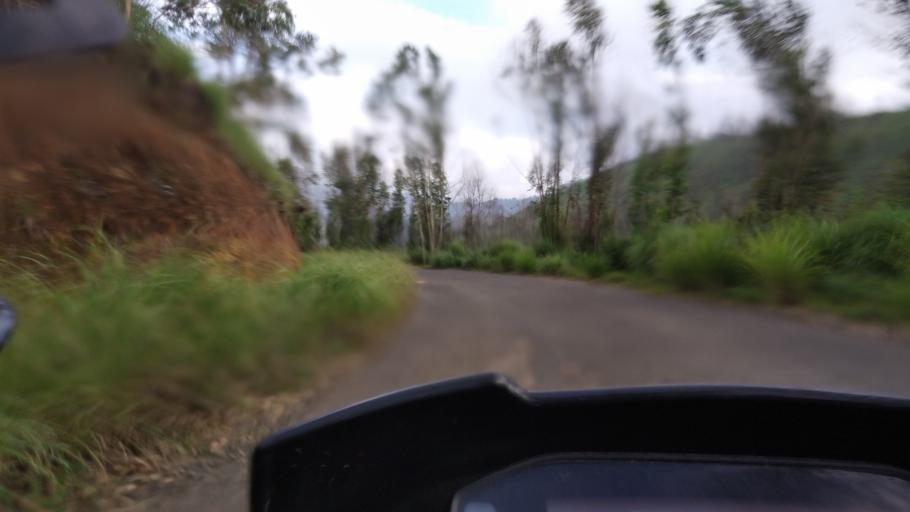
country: IN
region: Kerala
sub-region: Idukki
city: Munnar
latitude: 10.0370
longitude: 77.1849
